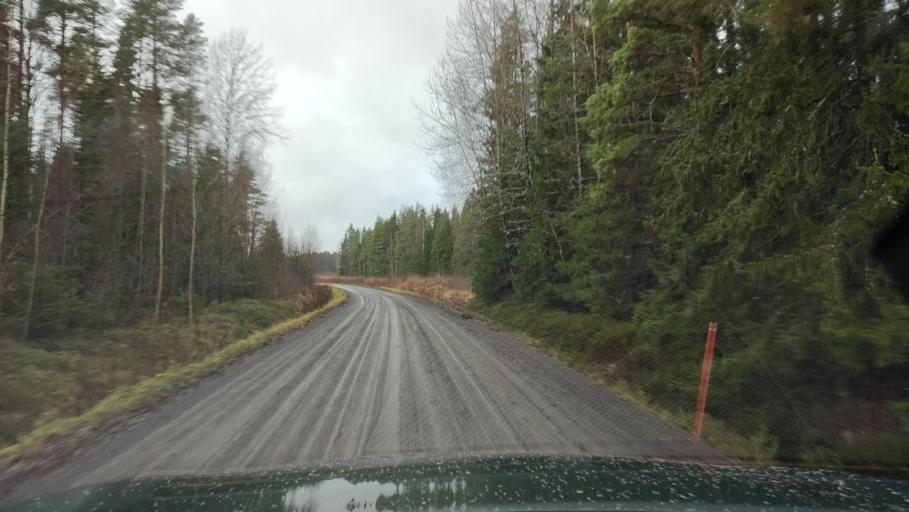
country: FI
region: Ostrobothnia
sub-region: Sydosterbotten
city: Naerpes
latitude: 62.4565
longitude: 21.5110
